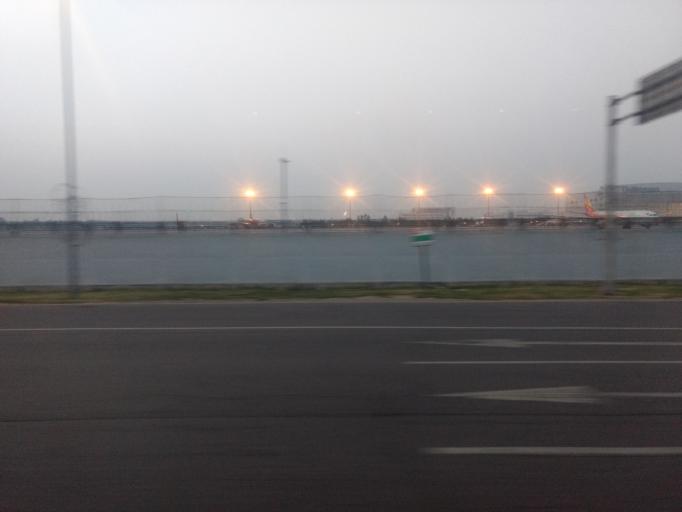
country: CN
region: Beijing
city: Tianzhu
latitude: 40.0879
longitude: 116.5774
